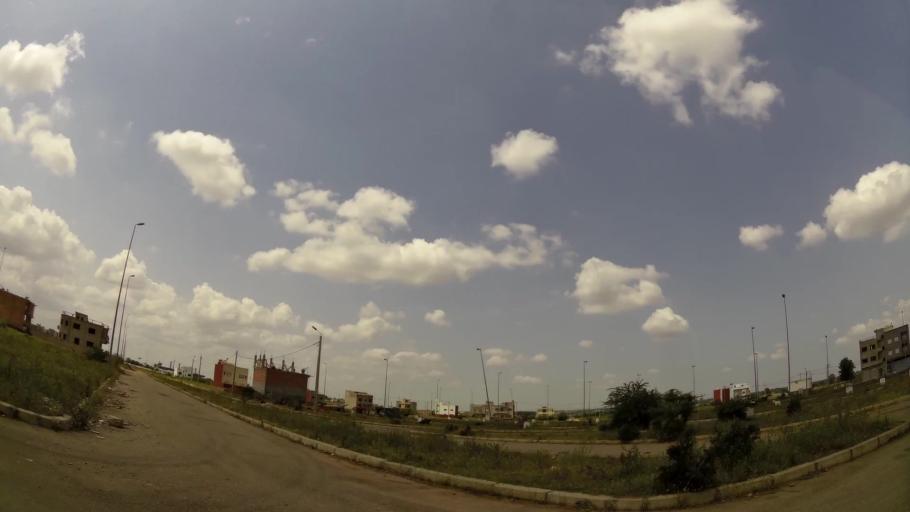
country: MA
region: Rabat-Sale-Zemmour-Zaer
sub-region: Khemisset
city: Tiflet
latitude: 34.0047
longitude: -6.5390
